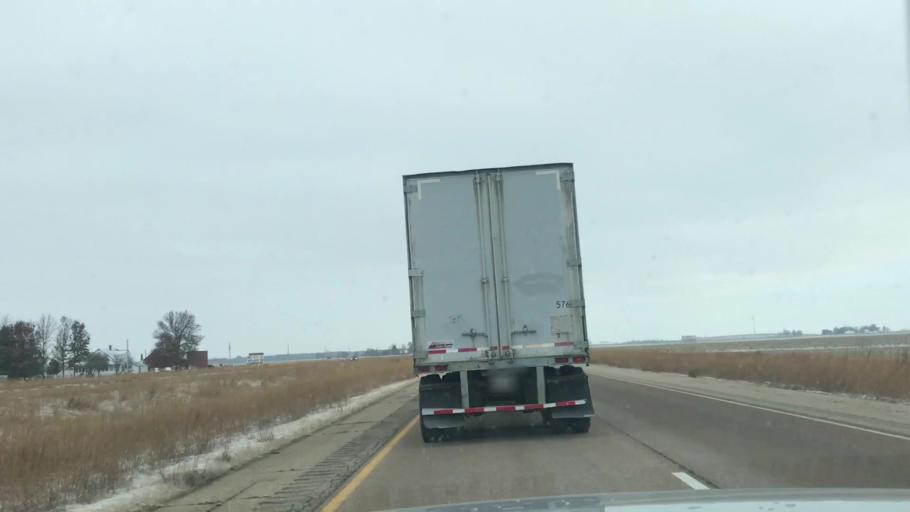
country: US
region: Illinois
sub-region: Montgomery County
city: Raymond
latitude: 39.4003
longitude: -89.6431
